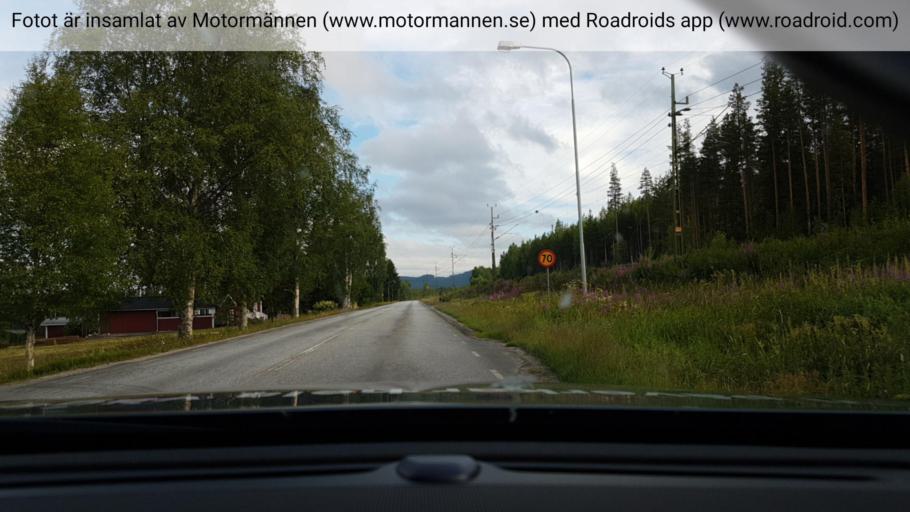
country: SE
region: Vaesterbotten
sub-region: Vindelns Kommun
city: Vindeln
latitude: 64.2181
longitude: 19.7093
